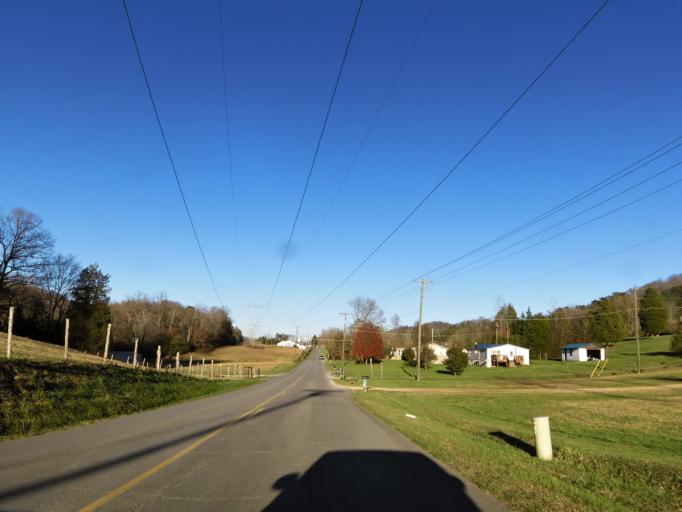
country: US
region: Tennessee
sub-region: Anderson County
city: Clinton
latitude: 36.0979
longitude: -84.2262
